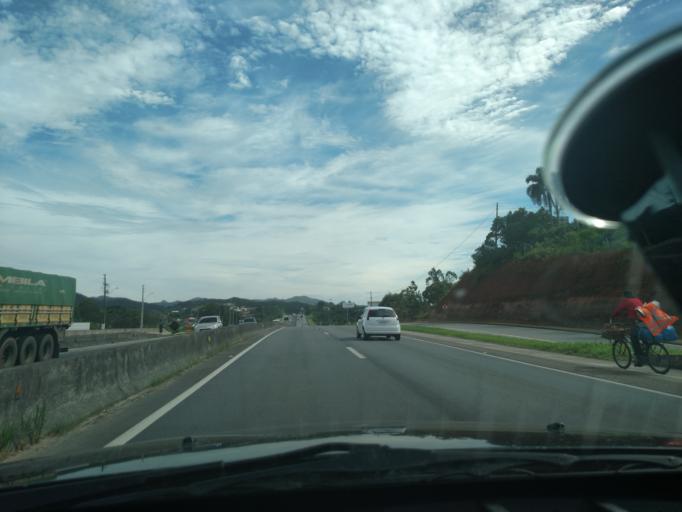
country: BR
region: Santa Catarina
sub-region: Biguacu
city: Biguacu
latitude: -27.4009
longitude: -48.6297
